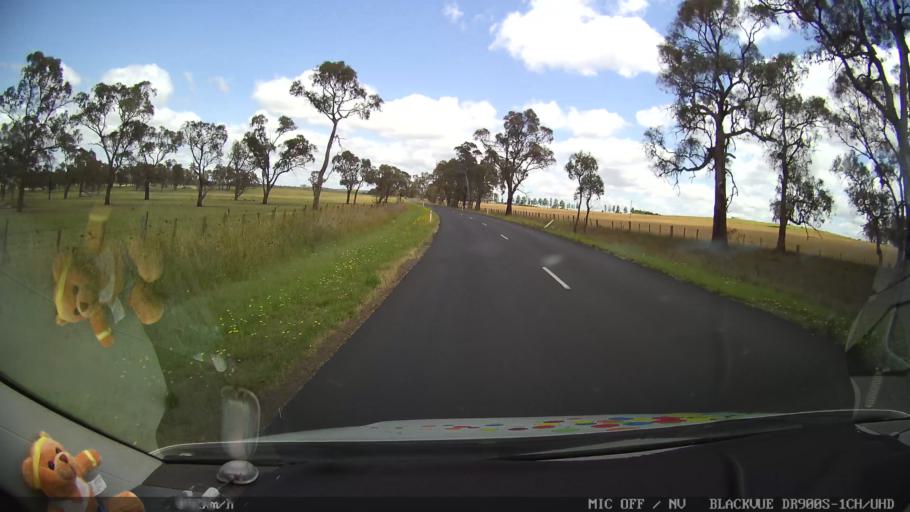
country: AU
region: New South Wales
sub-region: Glen Innes Severn
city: Glen Innes
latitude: -29.6514
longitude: 151.6933
